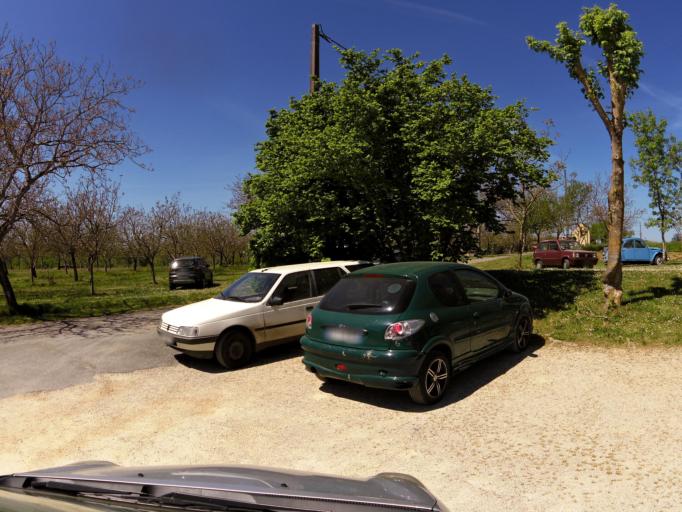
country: FR
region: Aquitaine
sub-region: Departement de la Dordogne
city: Carsac-Aillac
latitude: 44.8285
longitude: 1.2514
